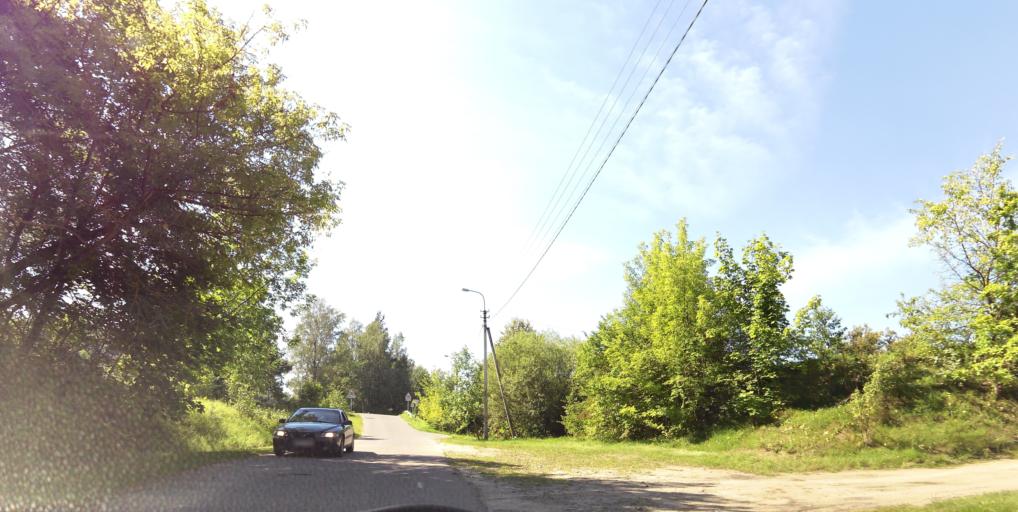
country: LT
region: Vilnius County
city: Rasos
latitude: 54.6771
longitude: 25.3500
